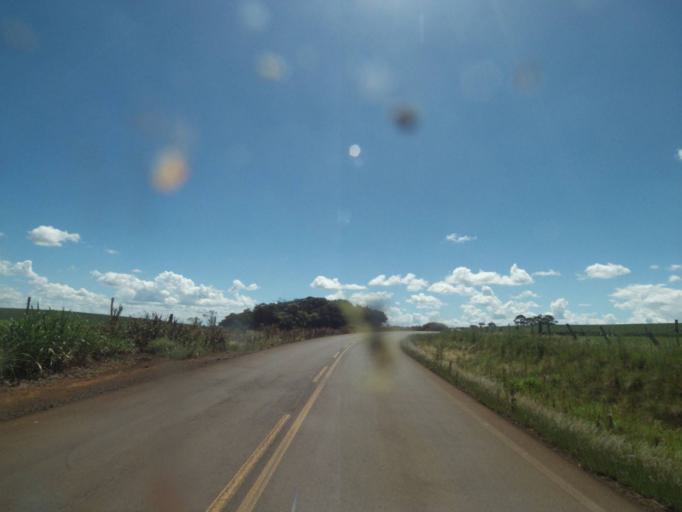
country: BR
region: Parana
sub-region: Pinhao
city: Pinhao
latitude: -25.8132
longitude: -52.0652
